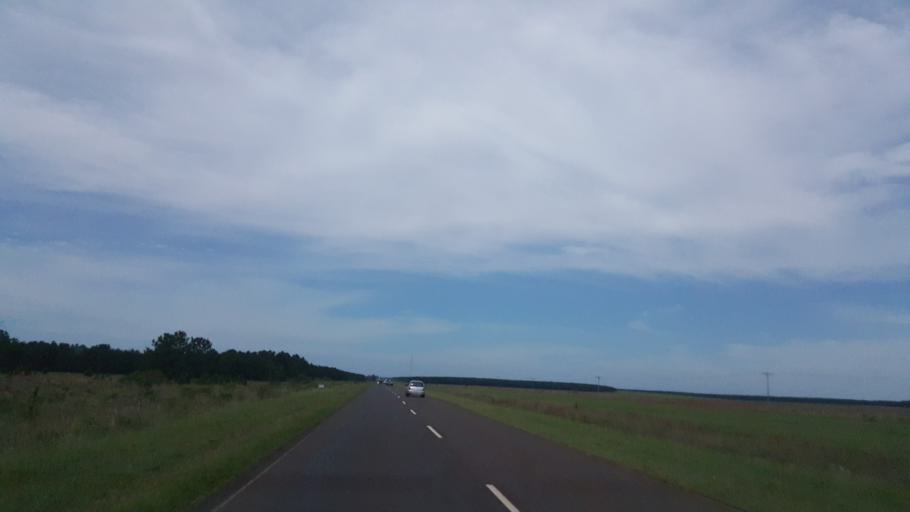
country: PY
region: Itapua
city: San Juan del Parana
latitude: -27.5098
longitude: -56.1339
